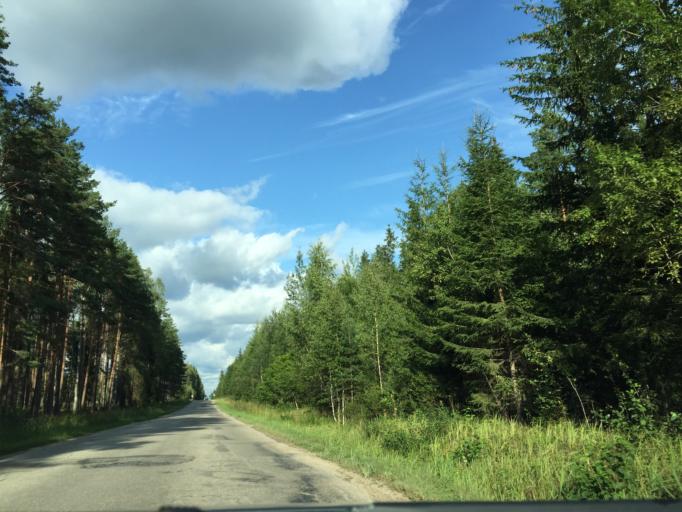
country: LV
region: Ogre
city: Ogre
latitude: 56.8327
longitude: 24.6517
